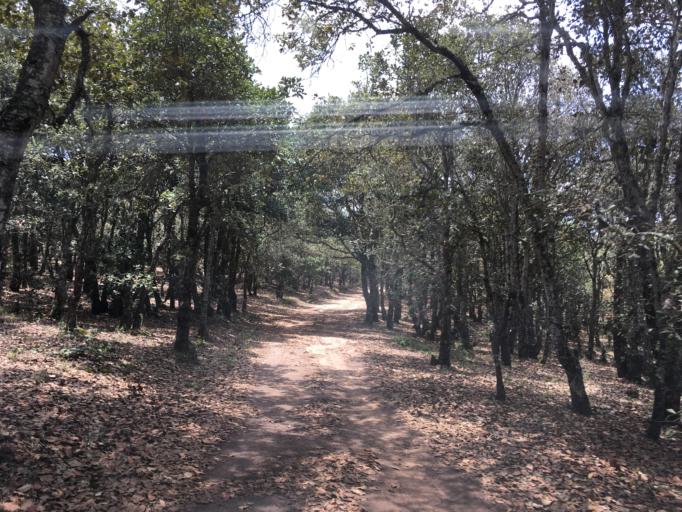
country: MX
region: Oaxaca
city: San Andres Sinaxtla
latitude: 17.6051
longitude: -97.2665
